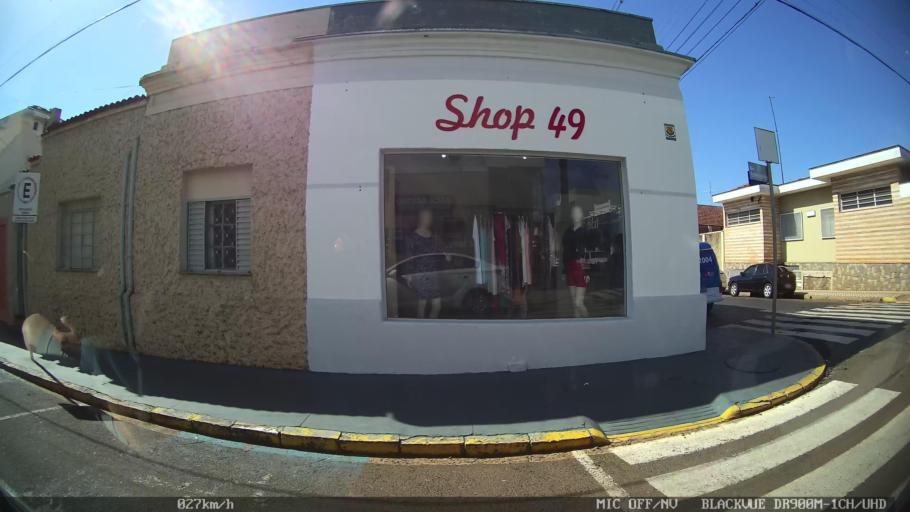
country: BR
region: Sao Paulo
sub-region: Batatais
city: Batatais
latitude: -20.8908
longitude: -47.5831
